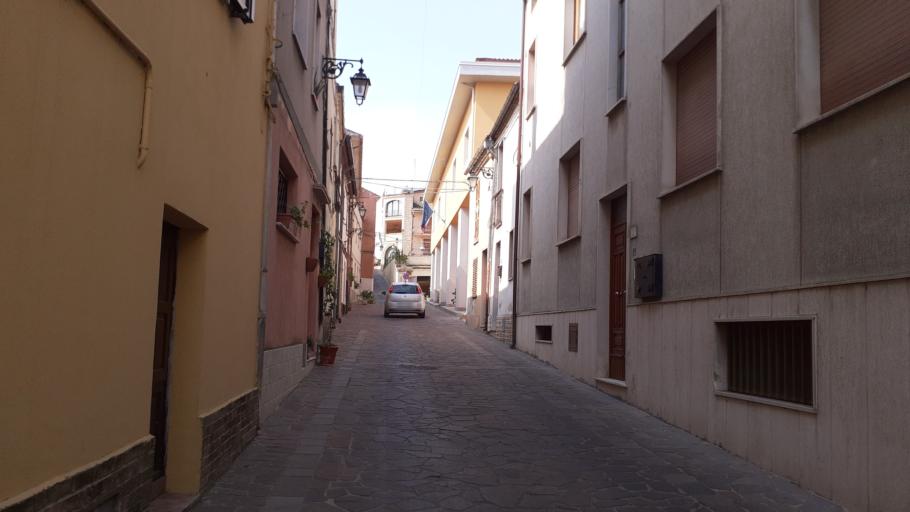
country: IT
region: Abruzzo
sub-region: Provincia di Chieti
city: Vacri
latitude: 42.2981
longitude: 14.2332
